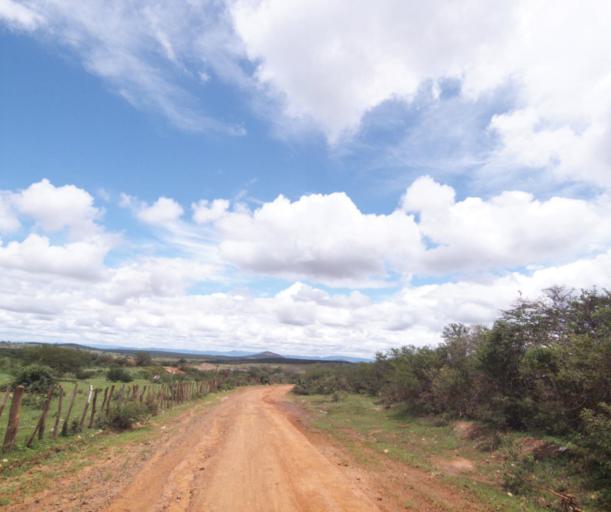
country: BR
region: Bahia
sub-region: Tanhacu
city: Tanhacu
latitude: -14.1881
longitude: -41.0810
